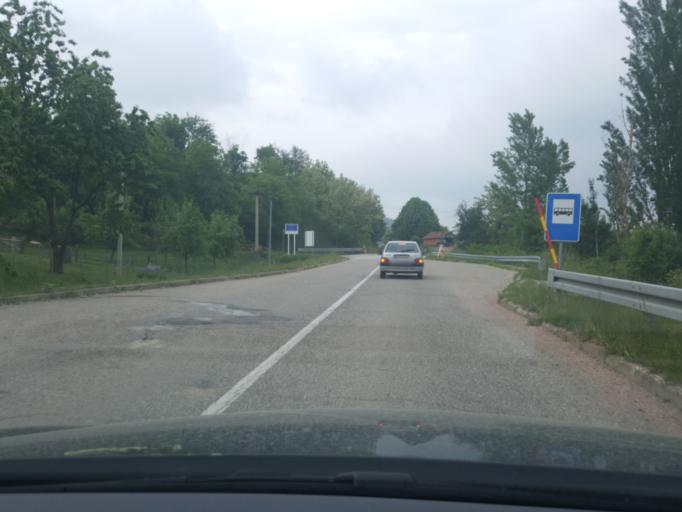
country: RS
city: Kamenica
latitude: 44.2159
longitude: 19.7155
